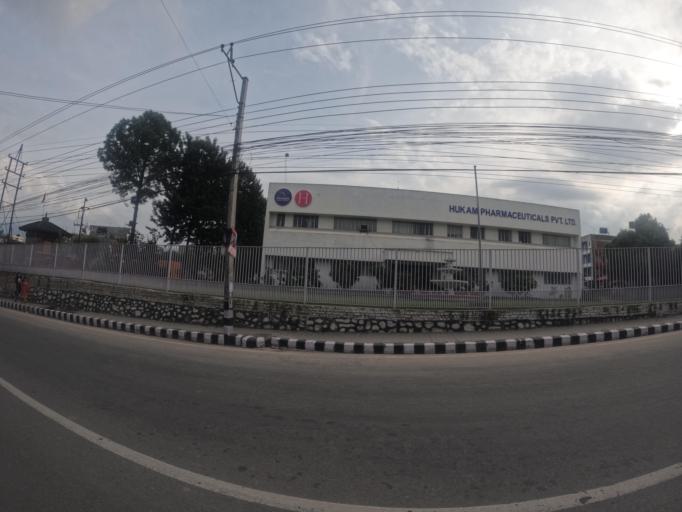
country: NP
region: Central Region
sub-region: Bagmati Zone
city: Bhaktapur
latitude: 27.6815
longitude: 85.3927
